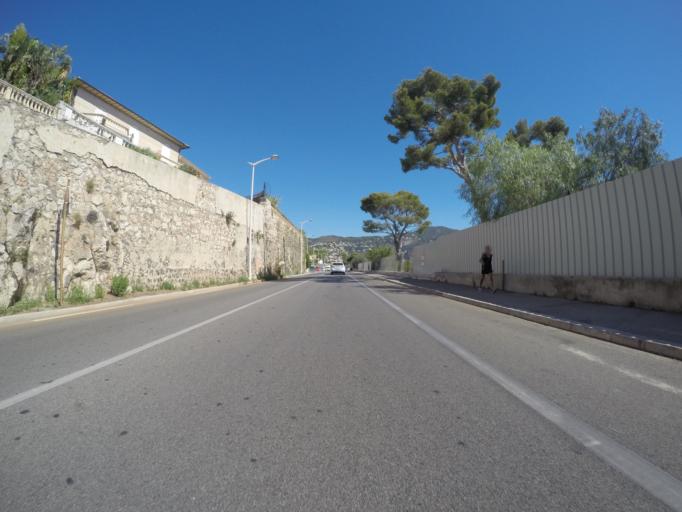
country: FR
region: Provence-Alpes-Cote d'Azur
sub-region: Departement des Alpes-Maritimes
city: Villefranche-sur-Mer
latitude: 43.6901
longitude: 7.3070
